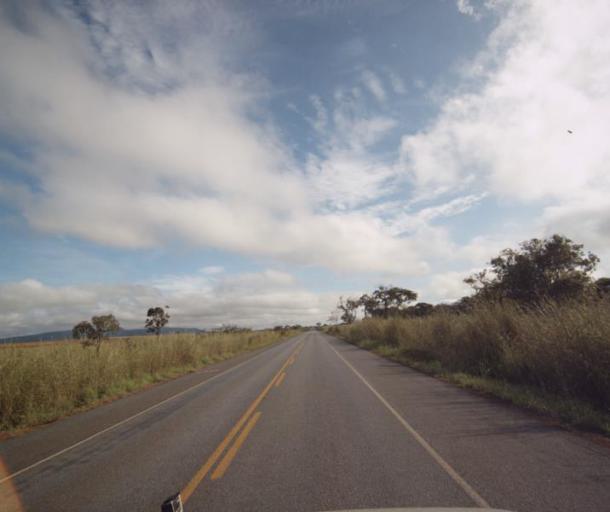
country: BR
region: Goias
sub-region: Padre Bernardo
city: Padre Bernardo
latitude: -15.4607
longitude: -48.6139
